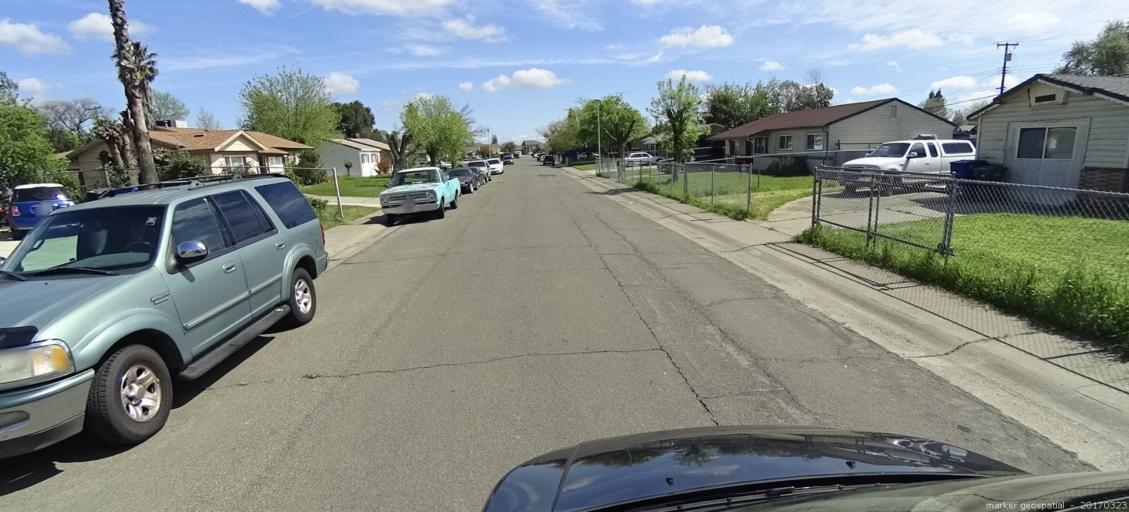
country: US
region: California
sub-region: Sacramento County
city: Florin
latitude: 38.5047
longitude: -121.4158
